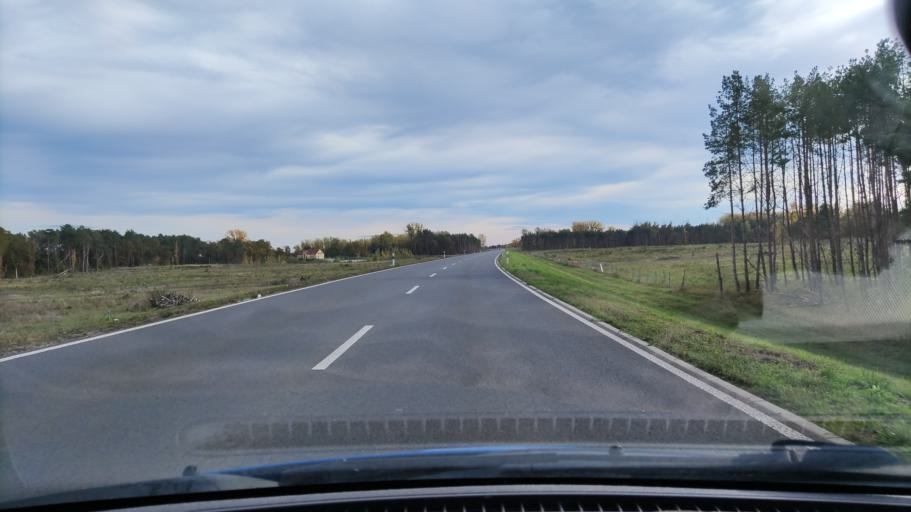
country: DE
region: Brandenburg
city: Breese
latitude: 53.0059
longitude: 11.7776
